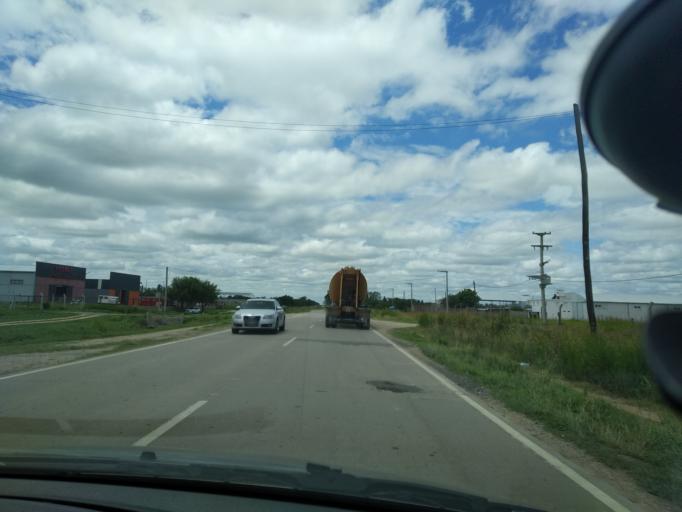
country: AR
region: Cordoba
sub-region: Departamento de Rio Segundo
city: Rio Segundo
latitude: -31.6400
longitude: -63.8940
